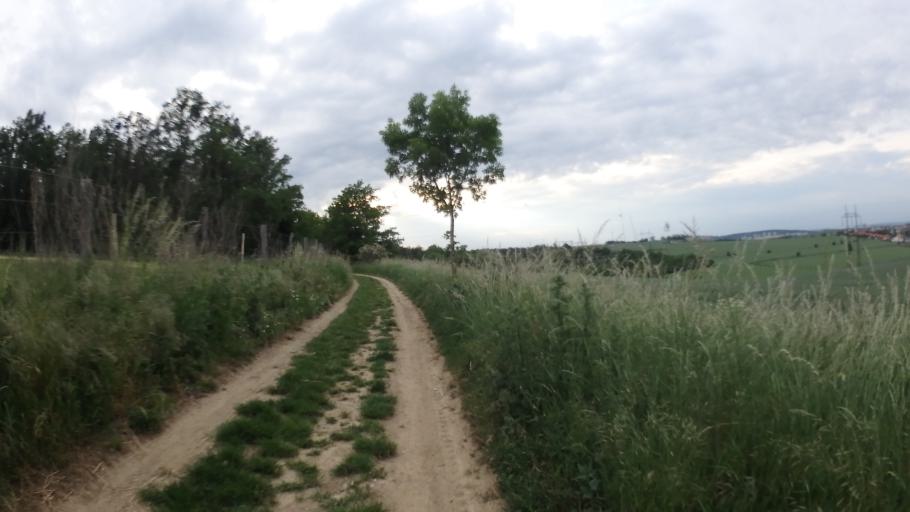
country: CZ
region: South Moravian
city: Moravany
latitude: 49.1373
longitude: 16.5684
